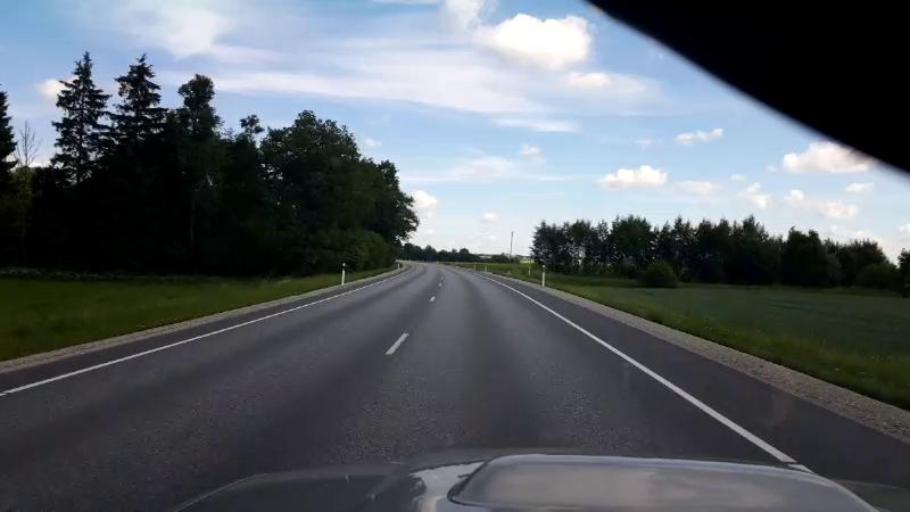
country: EE
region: Jaervamaa
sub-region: Jaerva-Jaani vald
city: Jarva-Jaani
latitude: 59.0157
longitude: 25.7010
